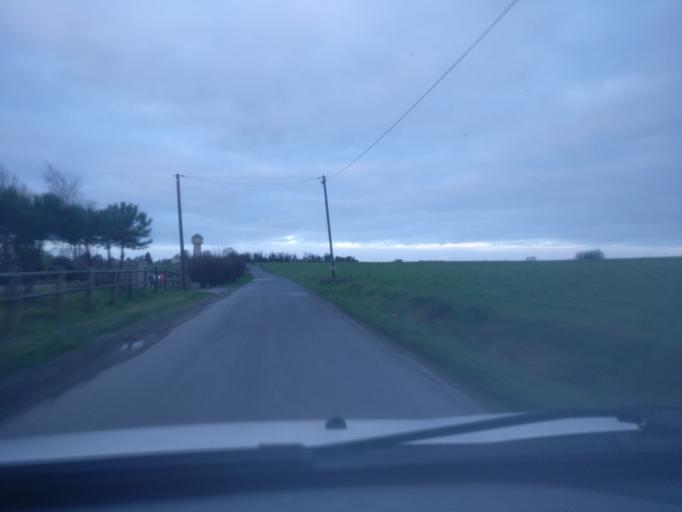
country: FR
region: Lower Normandy
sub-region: Departement de la Manche
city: Marcey-les-Greves
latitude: 48.6738
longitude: -1.4306
